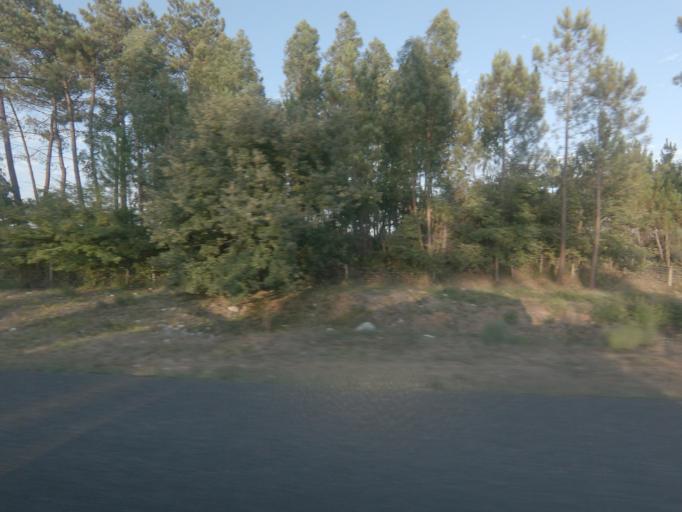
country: PT
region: Leiria
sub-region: Leiria
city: Santa Catarina da Serra
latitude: 39.6524
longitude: -8.6961
